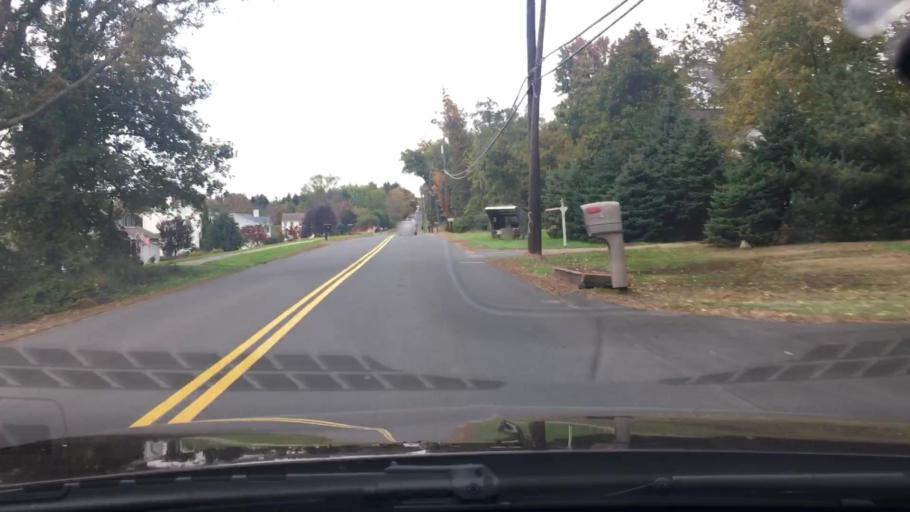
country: US
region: Connecticut
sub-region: Tolland County
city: Ellington
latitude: 41.9292
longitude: -72.4778
